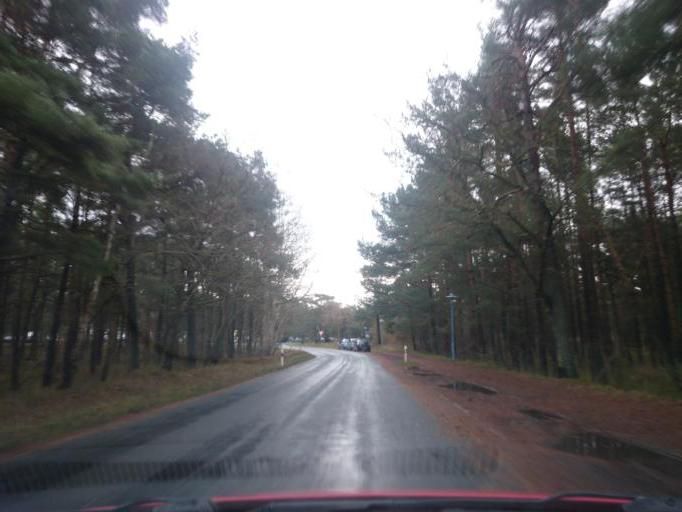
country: DE
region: Mecklenburg-Vorpommern
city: Altenkirchen
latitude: 54.6141
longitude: 13.3774
